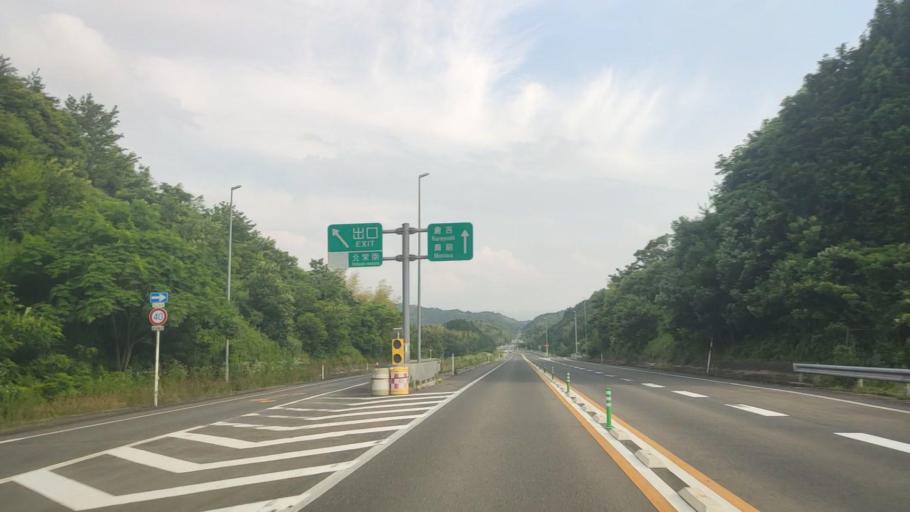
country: JP
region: Tottori
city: Kurayoshi
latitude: 35.4686
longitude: 133.8079
